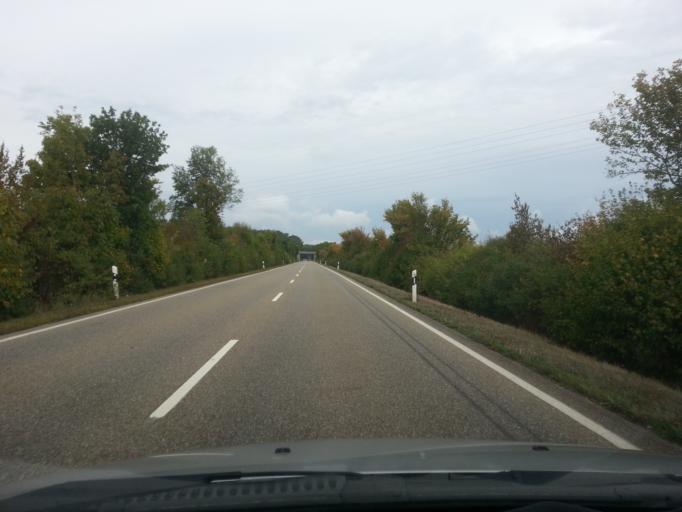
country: DE
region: Rheinland-Pfalz
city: Offenbach an der Queich
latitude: 49.1971
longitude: 8.1739
